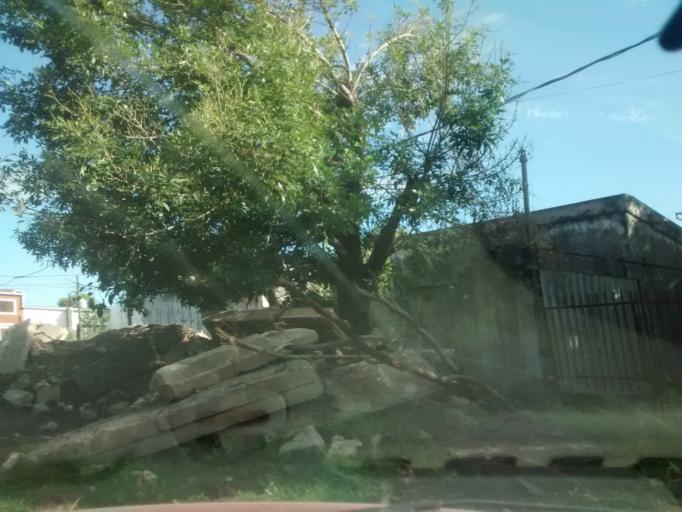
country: AR
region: Chaco
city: Puerto Tirol
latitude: -27.3715
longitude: -59.0960
